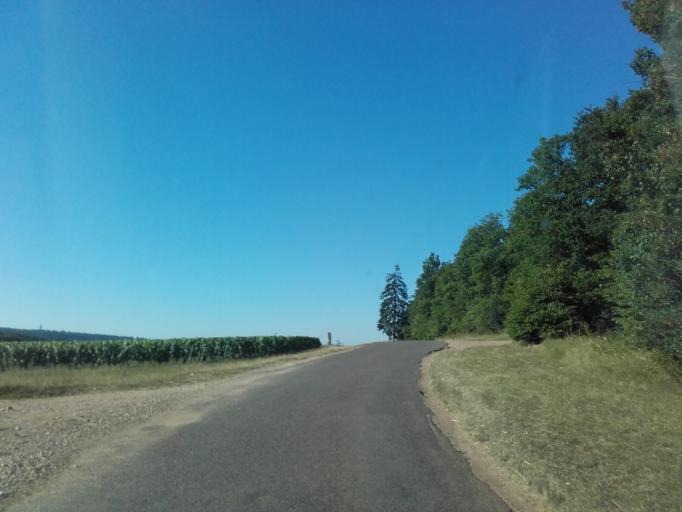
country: FR
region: Bourgogne
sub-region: Departement de Saone-et-Loire
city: Rully
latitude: 46.8494
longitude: 4.7382
